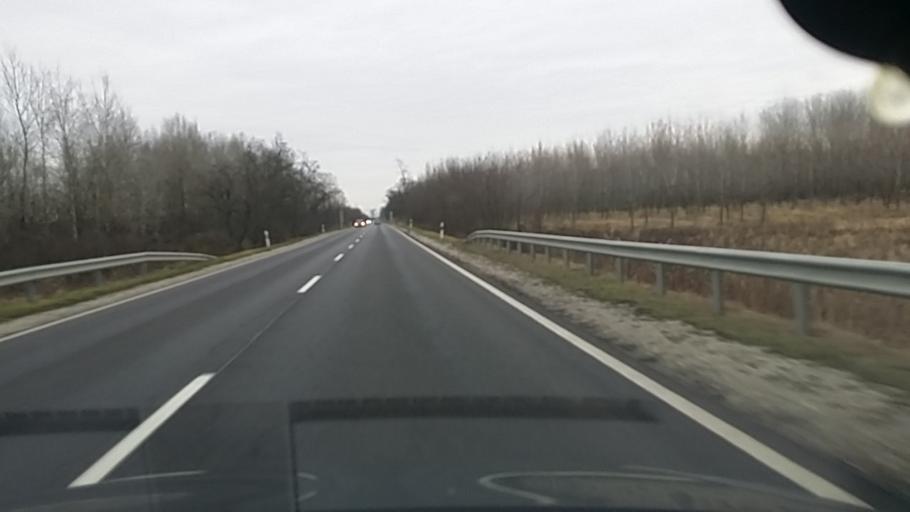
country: HU
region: Szabolcs-Szatmar-Bereg
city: Nyirbogdany
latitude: 48.0342
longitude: 21.8560
